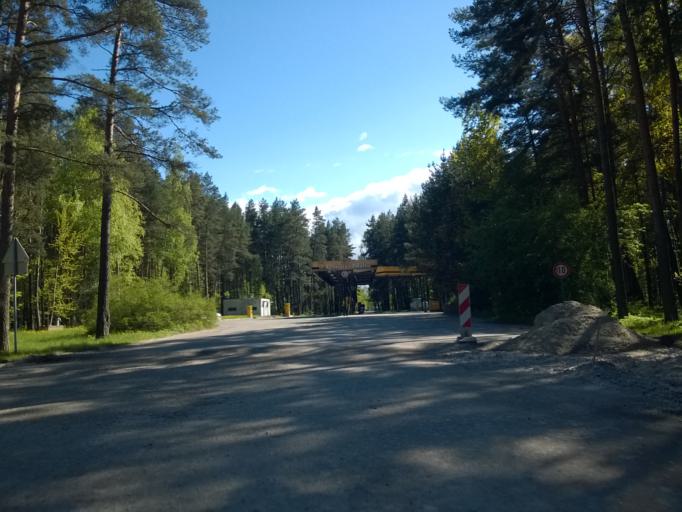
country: LV
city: Tireli
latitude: 56.9573
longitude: 23.6358
